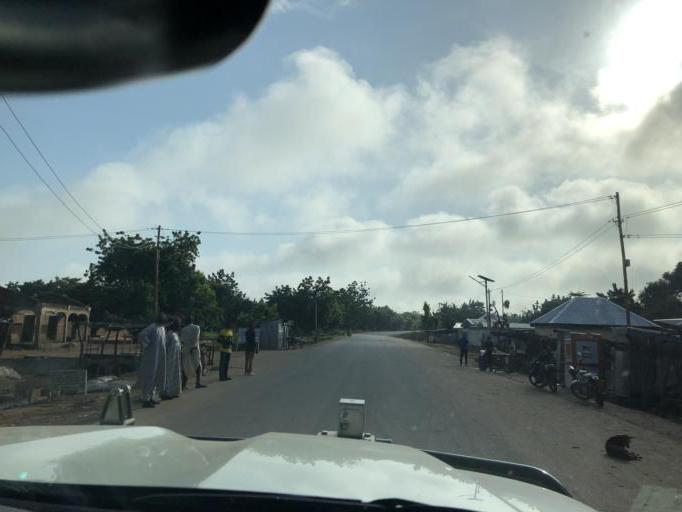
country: CM
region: North Province
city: Pitoa
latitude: 9.4936
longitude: 13.6834
